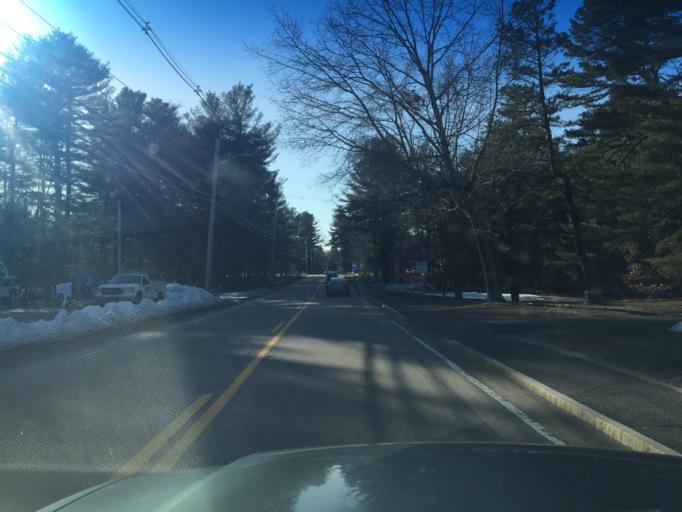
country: US
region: Massachusetts
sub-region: Norfolk County
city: Bellingham
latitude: 42.0866
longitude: -71.4855
